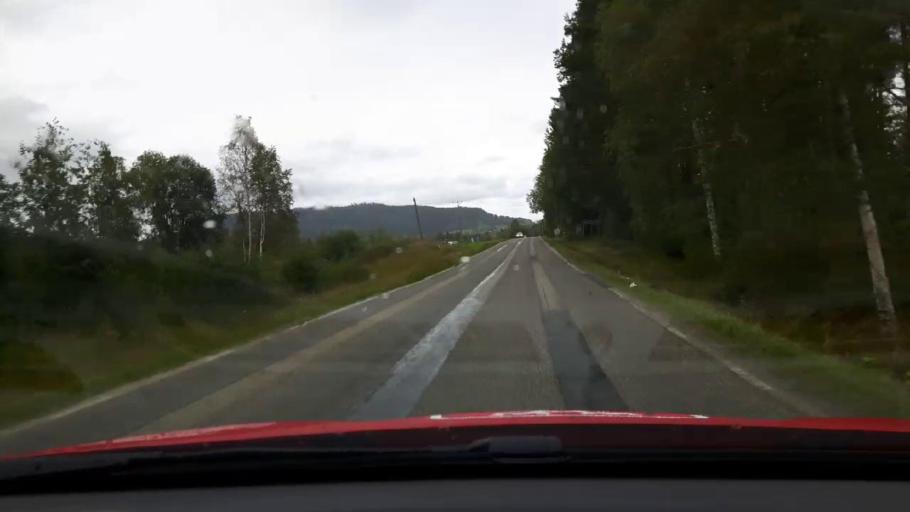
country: SE
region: Jaemtland
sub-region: Bergs Kommun
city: Hoverberg
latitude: 62.7945
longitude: 14.4371
